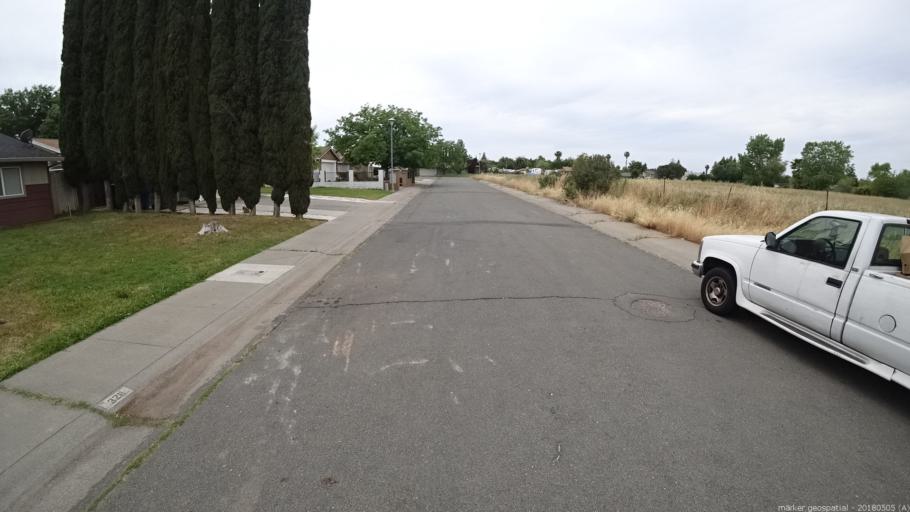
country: US
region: California
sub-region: Sacramento County
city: Rio Linda
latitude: 38.6507
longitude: -121.4594
